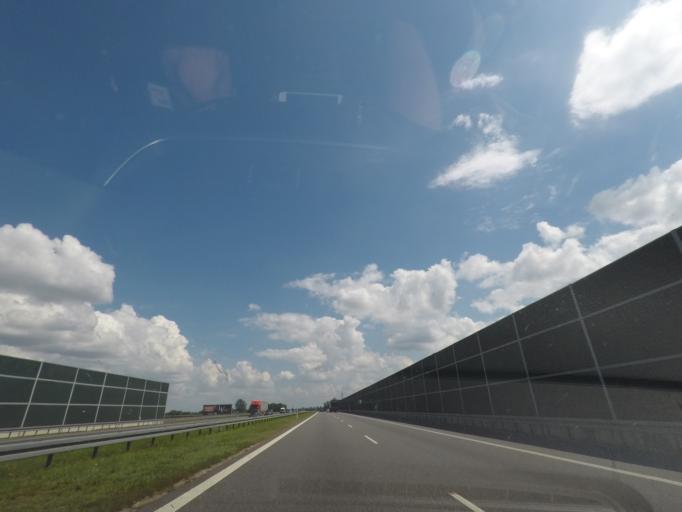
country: PL
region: Masovian Voivodeship
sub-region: Powiat zyrardowski
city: Wiskitki
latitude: 52.0990
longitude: 20.4133
